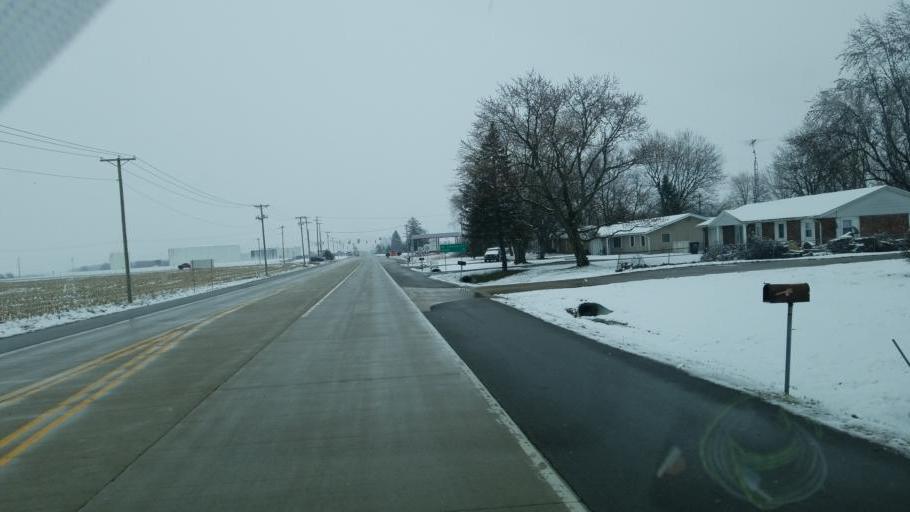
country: US
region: Indiana
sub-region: Delaware County
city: Eaton
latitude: 40.2770
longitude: -85.3711
